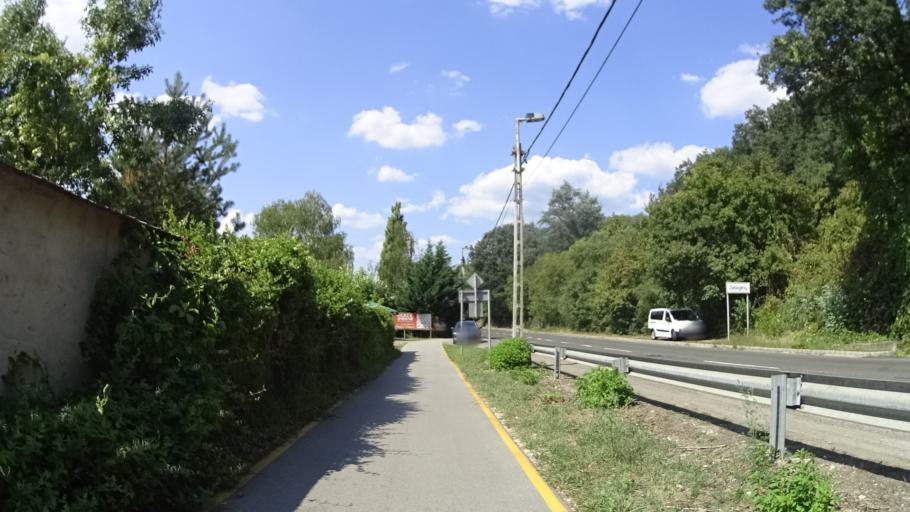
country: HU
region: Komarom-Esztergom
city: Pilismarot
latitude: 47.7835
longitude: 18.9115
